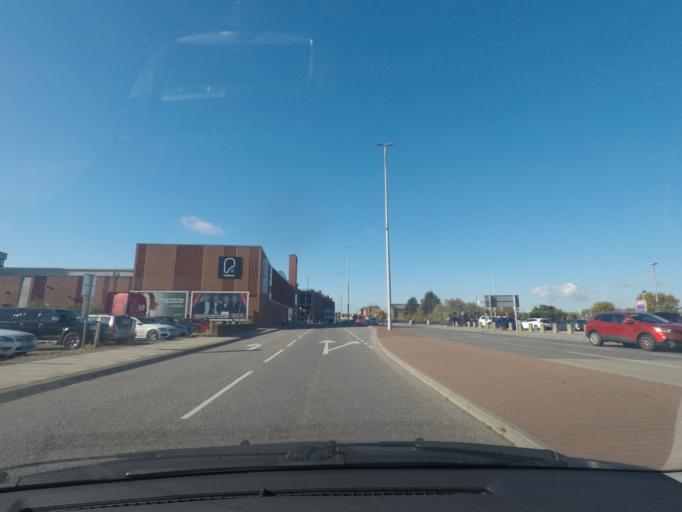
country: GB
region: England
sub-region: North East Lincolnshire
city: Grimsby
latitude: 53.5671
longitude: -0.0817
